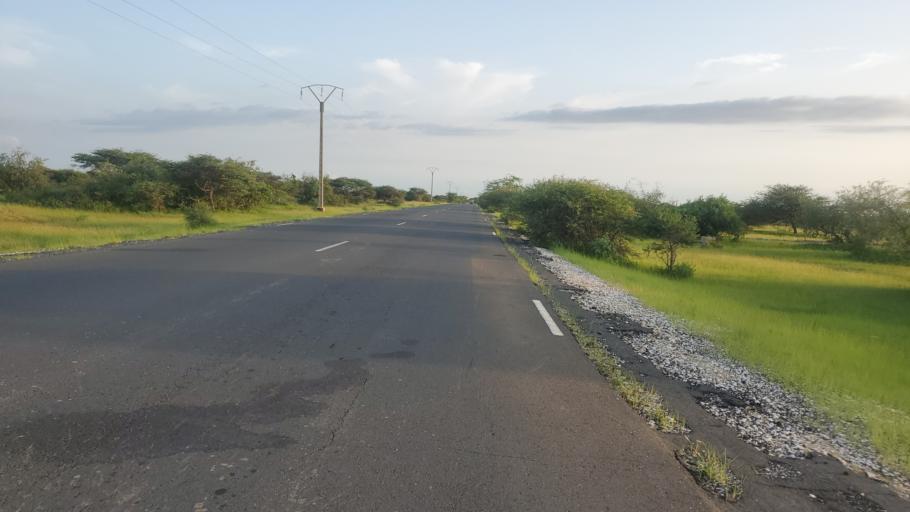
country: SN
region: Saint-Louis
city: Saint-Louis
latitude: 16.1777
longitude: -16.4096
